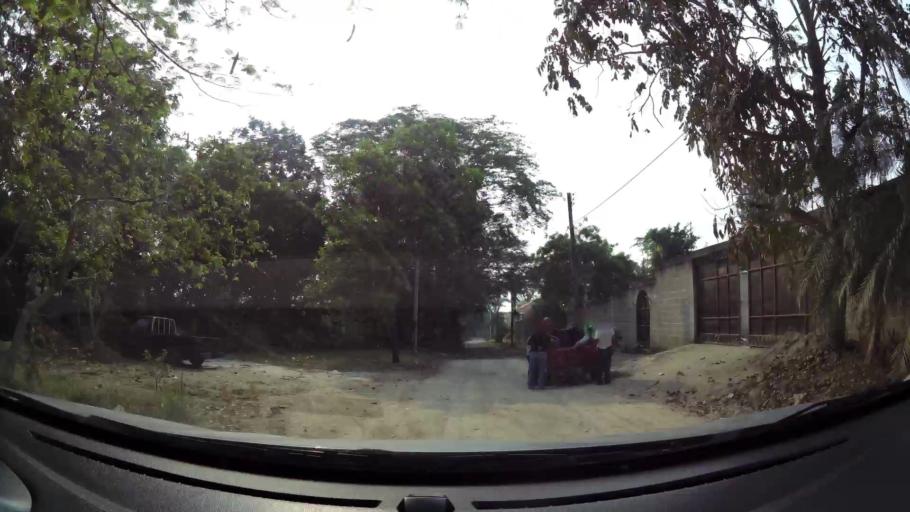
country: HN
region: Cortes
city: El Zapotal del Norte
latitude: 15.5196
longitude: -88.0448
